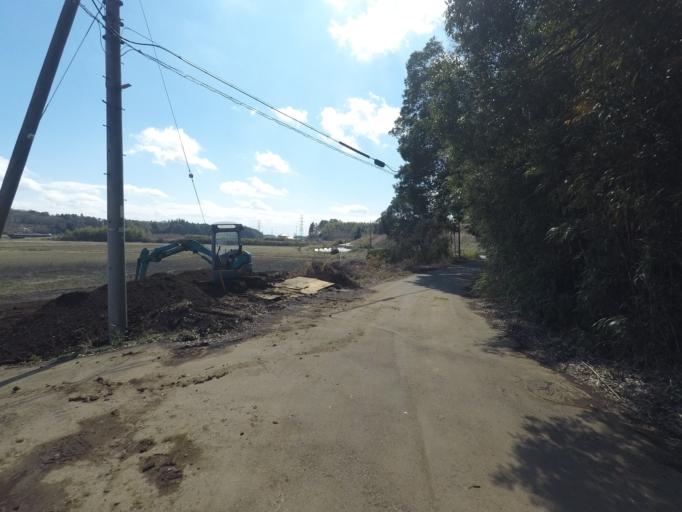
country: JP
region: Ibaraki
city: Ushiku
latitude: 36.0123
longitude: 140.0739
